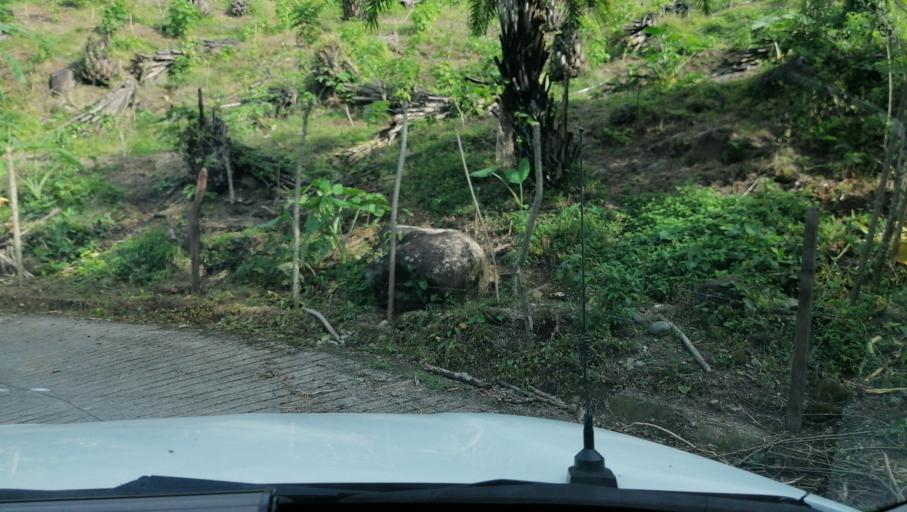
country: MX
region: Chiapas
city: Ostuacan
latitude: 17.4571
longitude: -93.2416
